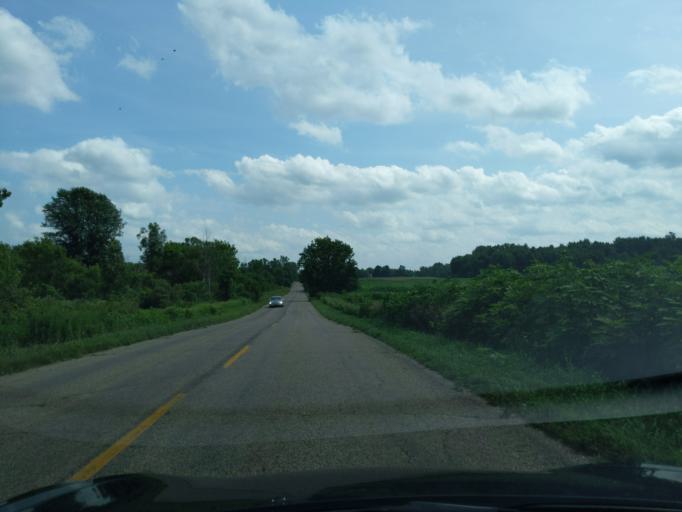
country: US
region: Michigan
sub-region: Eaton County
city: Eaton Rapids
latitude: 42.5492
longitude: -84.6019
